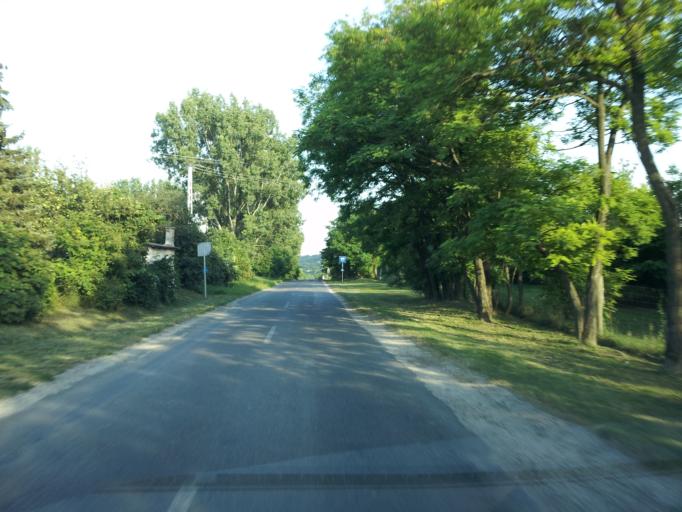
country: HU
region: Fejer
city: Many
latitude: 47.5312
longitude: 18.5953
